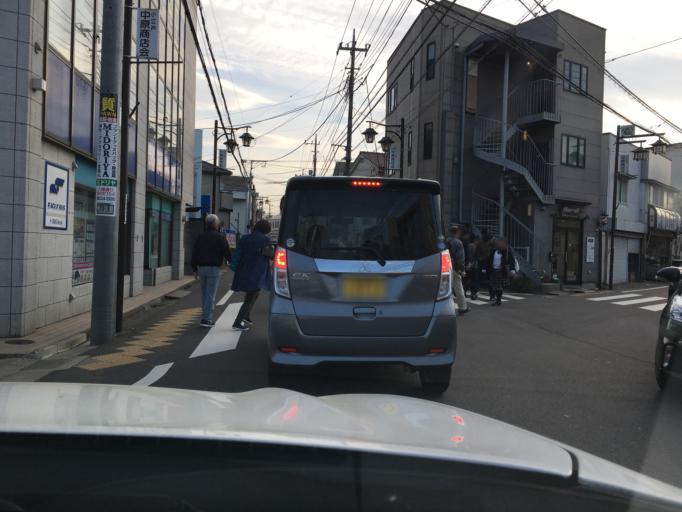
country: JP
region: Saitama
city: Kawagoe
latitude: 35.9143
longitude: 139.4798
